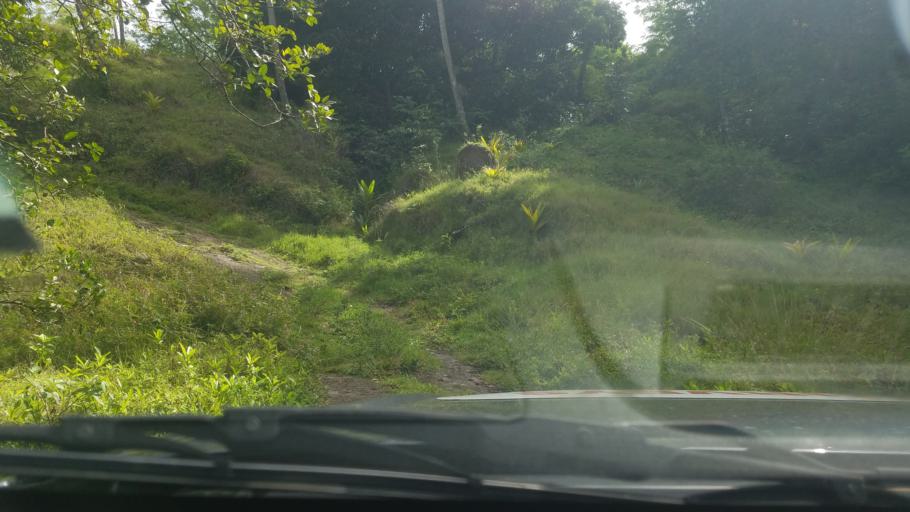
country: LC
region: Anse-la-Raye
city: Canaries
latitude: 13.8907
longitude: -61.0706
